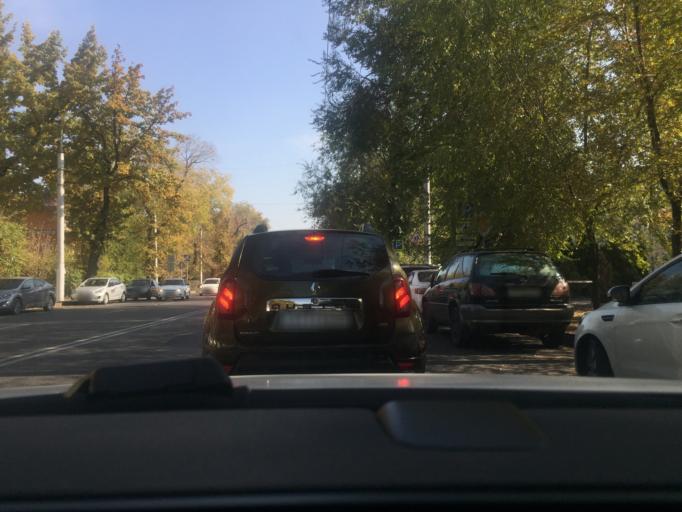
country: KZ
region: Almaty Qalasy
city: Almaty
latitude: 43.2589
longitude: 76.9299
